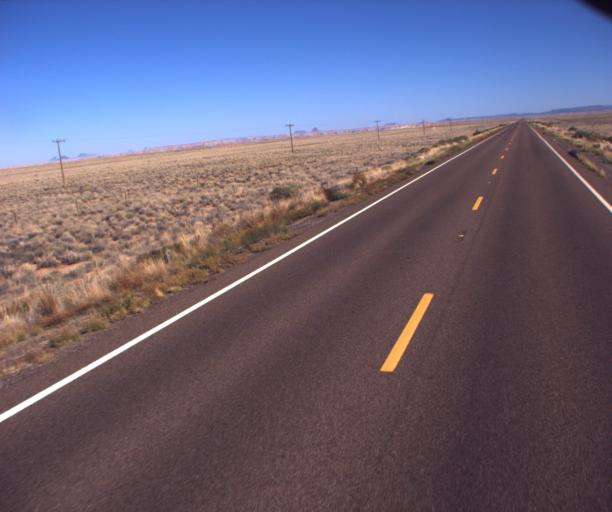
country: US
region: Arizona
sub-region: Navajo County
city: Winslow
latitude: 35.0987
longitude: -110.5367
